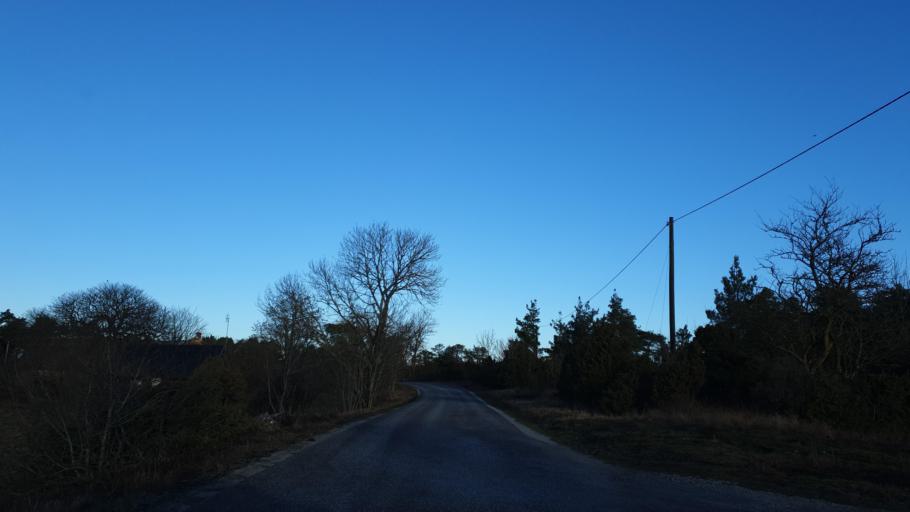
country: SE
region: Gotland
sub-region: Gotland
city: Slite
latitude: 57.3903
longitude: 18.8090
